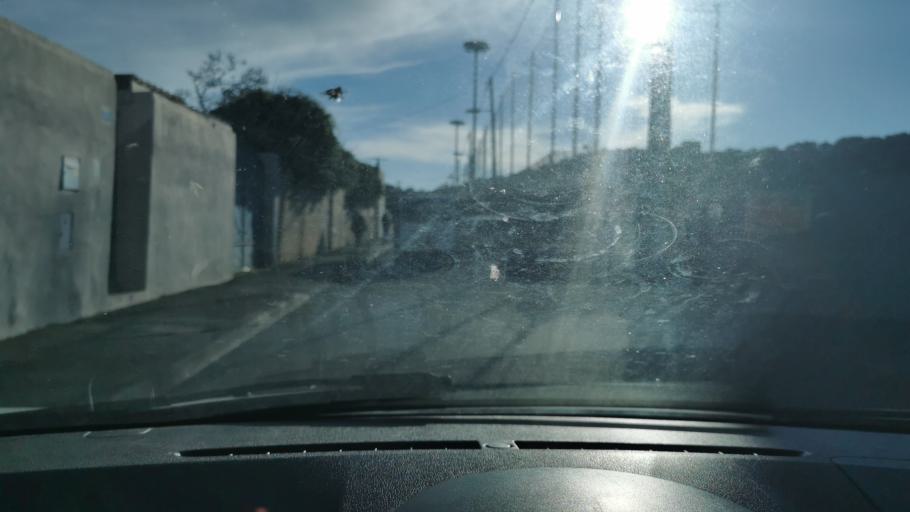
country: FR
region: Languedoc-Roussillon
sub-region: Departement de l'Herault
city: Sete
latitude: 43.4131
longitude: 3.6732
